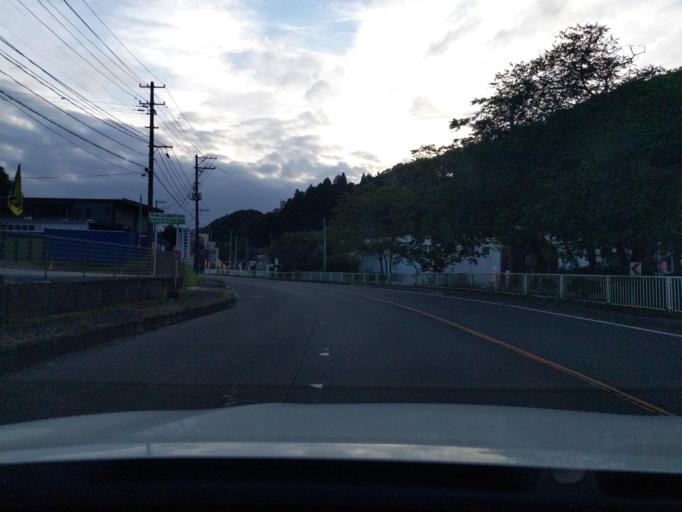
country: JP
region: Miyagi
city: Sendai
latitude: 38.2673
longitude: 140.8284
